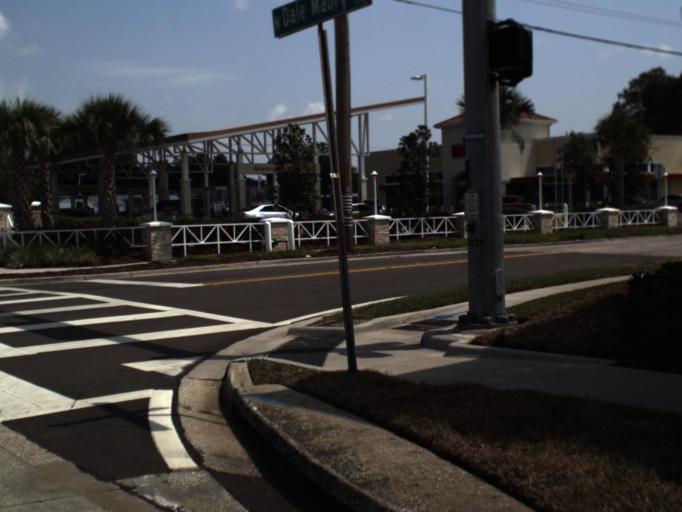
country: US
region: Florida
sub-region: Hillsborough County
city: Tampa
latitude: 27.9484
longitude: -82.5056
